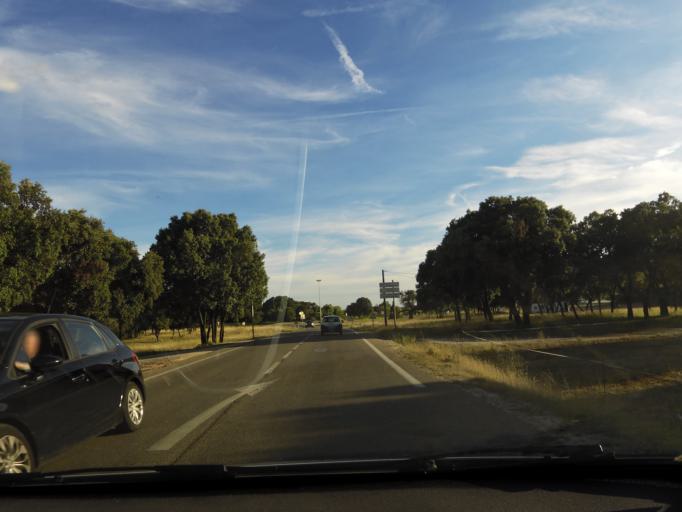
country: FR
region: Languedoc-Roussillon
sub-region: Departement de l'Herault
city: Saint-Mathieu-de-Treviers
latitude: 43.7763
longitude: 3.8704
